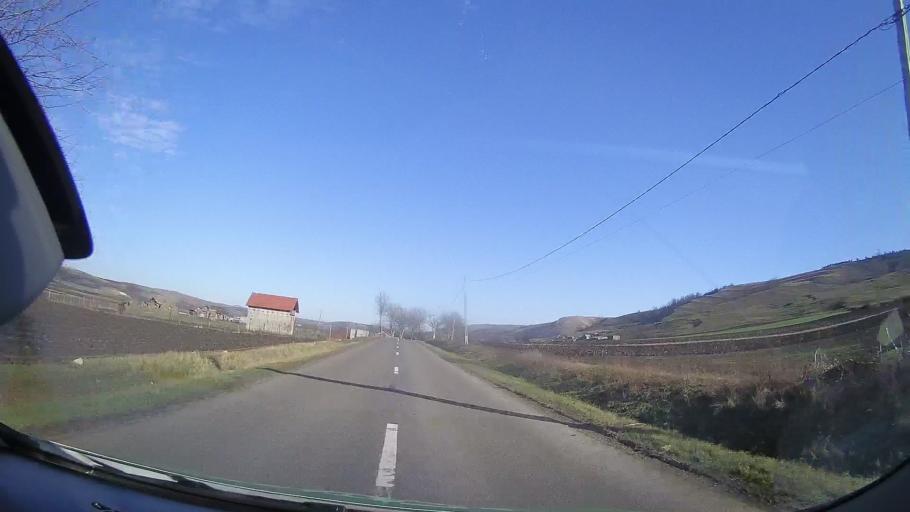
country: RO
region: Mures
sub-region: Comuna Iclanzel
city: Iclanzel
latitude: 46.5457
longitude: 24.3234
